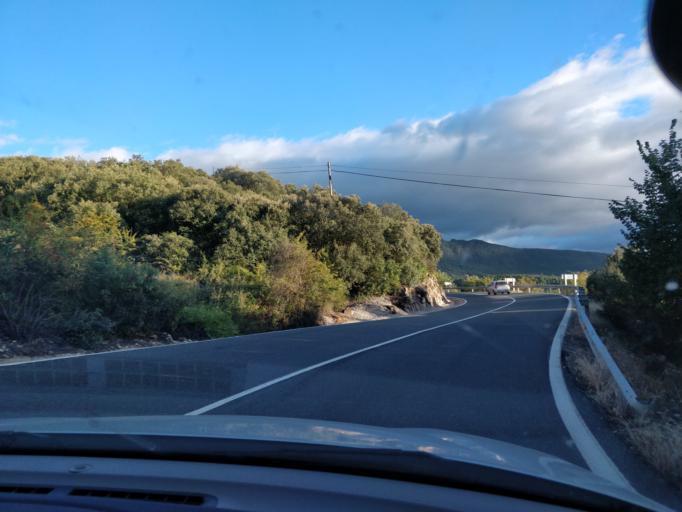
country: ES
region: Castille and Leon
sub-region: Provincia de Leon
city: Borrenes
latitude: 42.4976
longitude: -6.7191
